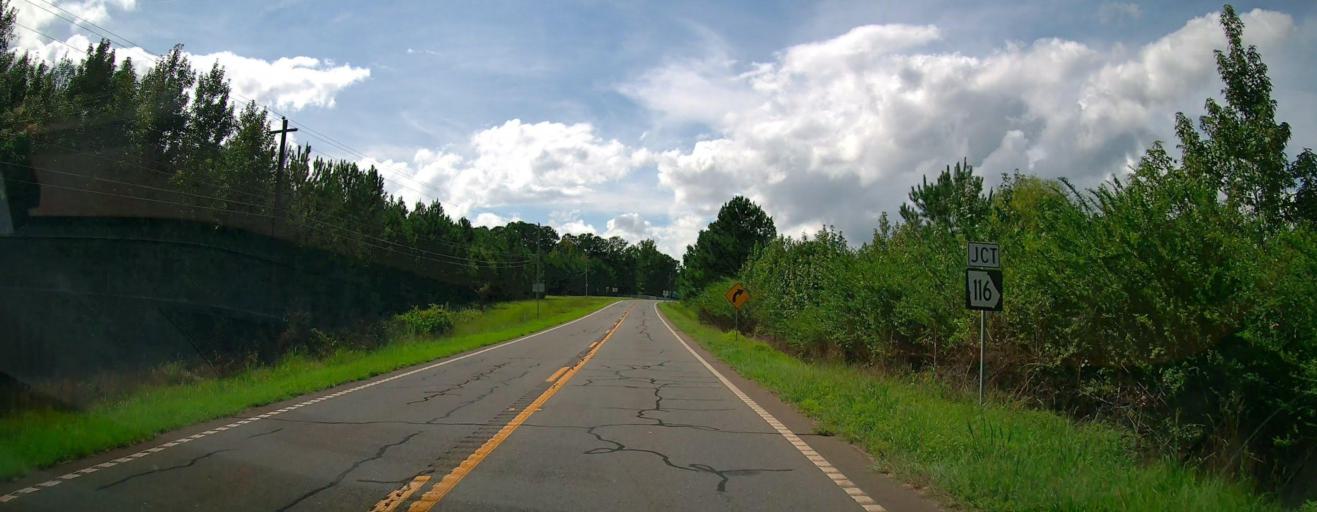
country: US
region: Georgia
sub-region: Talbot County
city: Sardis
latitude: 32.8000
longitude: -84.5848
